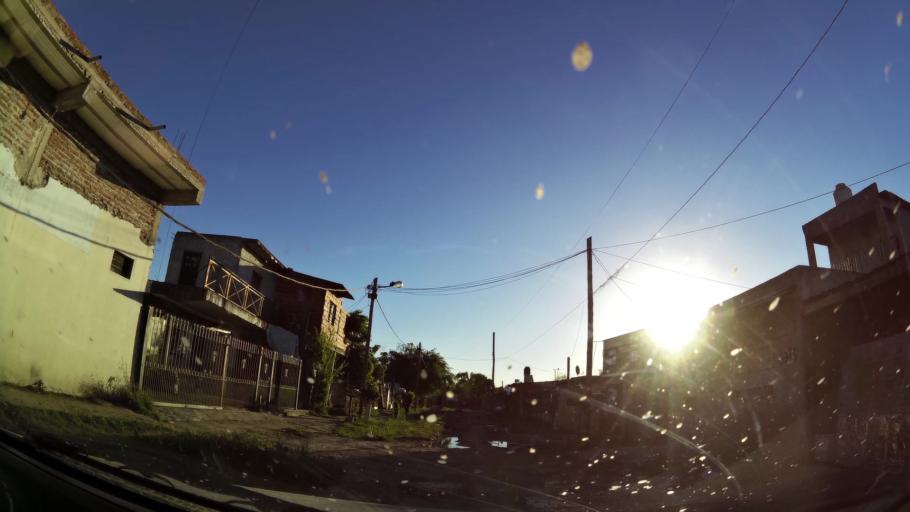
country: AR
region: Buenos Aires
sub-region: Partido de Almirante Brown
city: Adrogue
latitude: -34.7709
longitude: -58.3285
